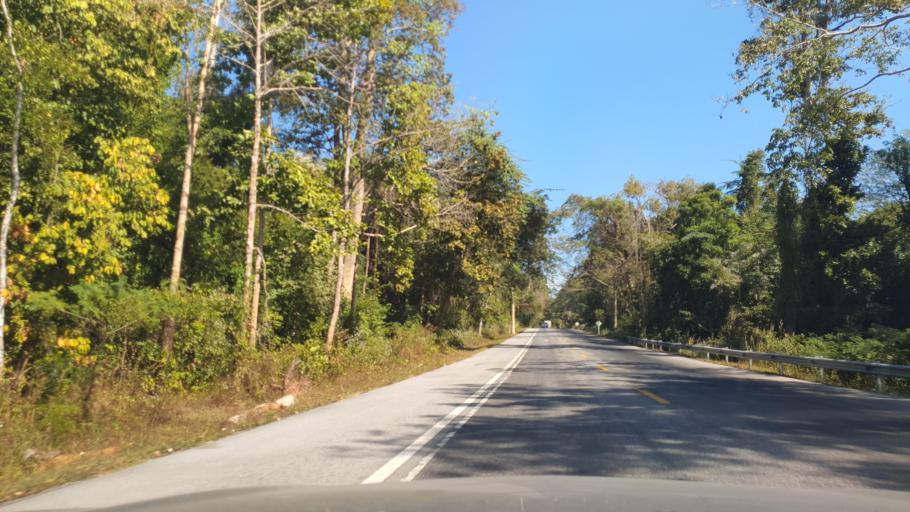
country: TH
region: Kalasin
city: Na Khu
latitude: 16.8484
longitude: 103.9234
